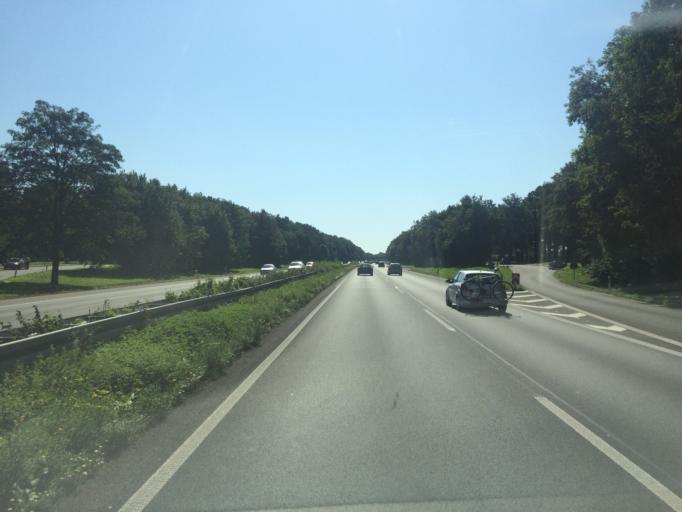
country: DE
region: North Rhine-Westphalia
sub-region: Regierungsbezirk Munster
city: Ascheberg
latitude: 51.7507
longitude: 7.6467
